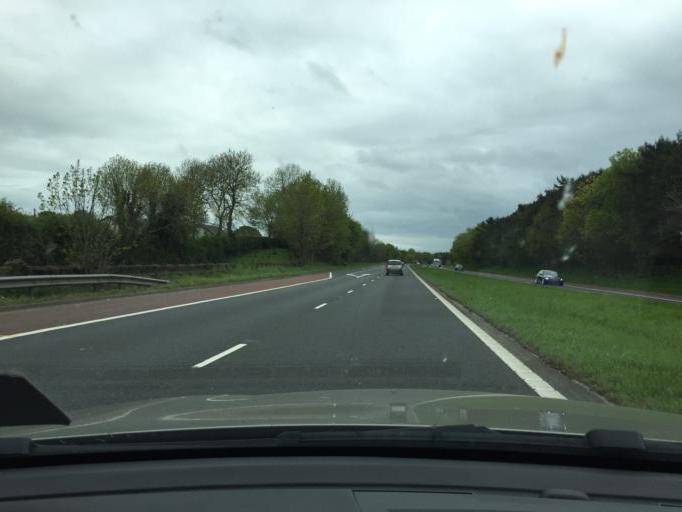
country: GB
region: Northern Ireland
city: Hillsborough
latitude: 54.4520
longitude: -6.1049
